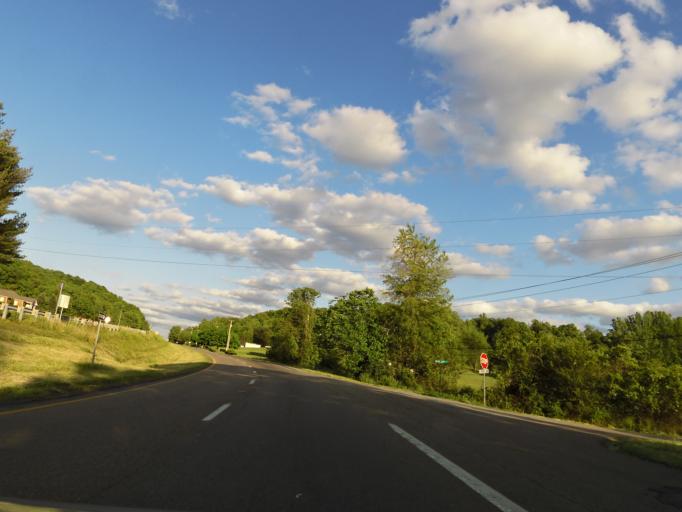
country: US
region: Virginia
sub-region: Washington County
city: Abingdon
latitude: 36.7303
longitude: -82.0357
